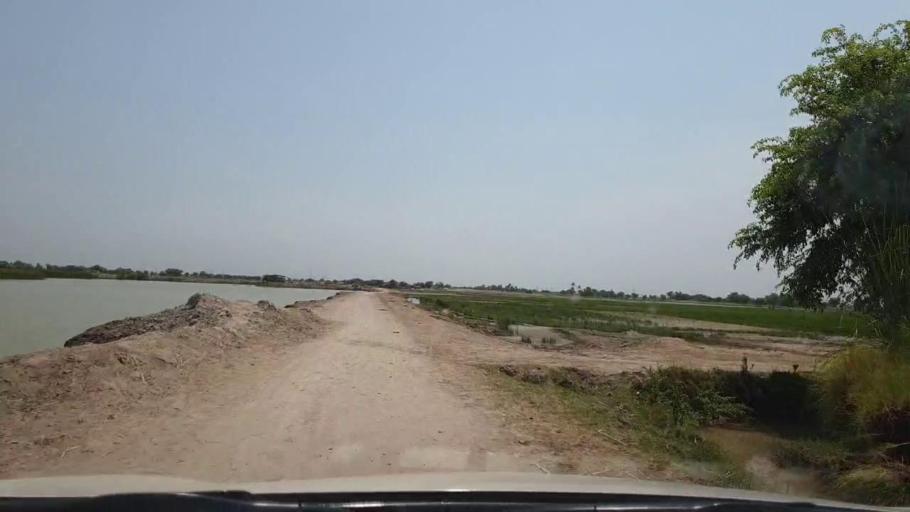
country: PK
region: Sindh
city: Ratodero
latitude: 27.8081
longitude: 68.2442
